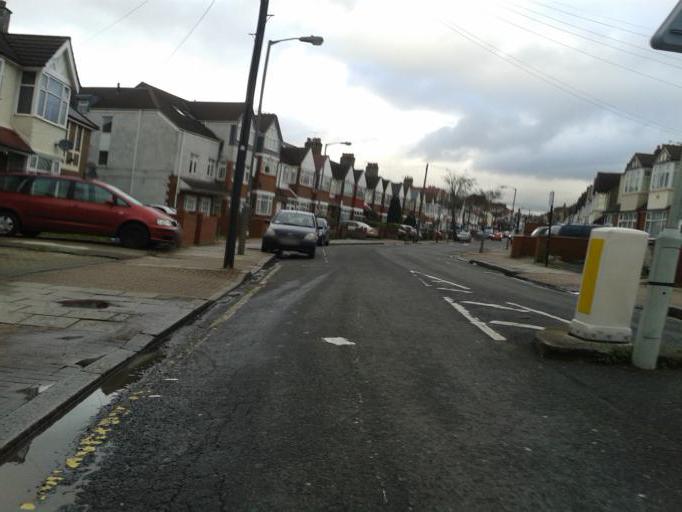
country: GB
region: England
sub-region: Greater London
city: Earlsfield
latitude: 51.4314
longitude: -0.1688
